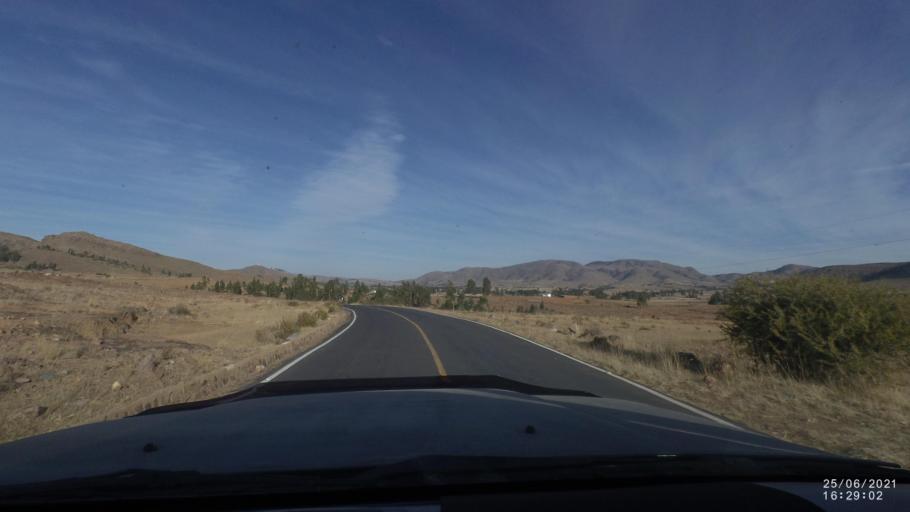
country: BO
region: Cochabamba
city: Arani
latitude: -17.7830
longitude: -65.8121
